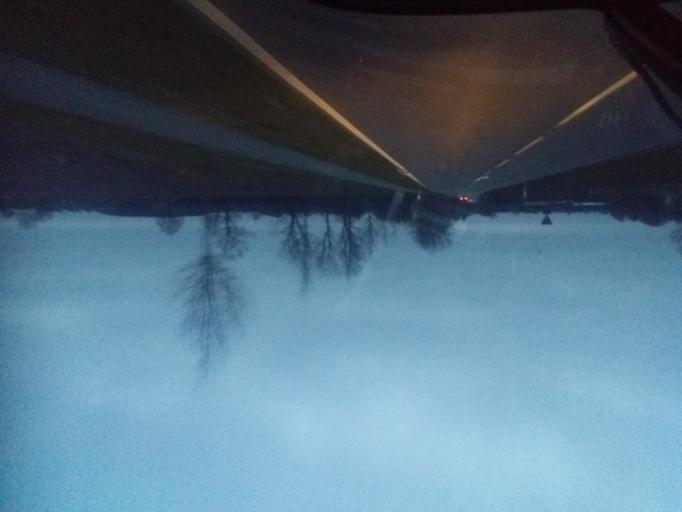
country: DE
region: Schleswig-Holstein
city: Poschendorf
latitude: 54.0316
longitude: 9.4779
